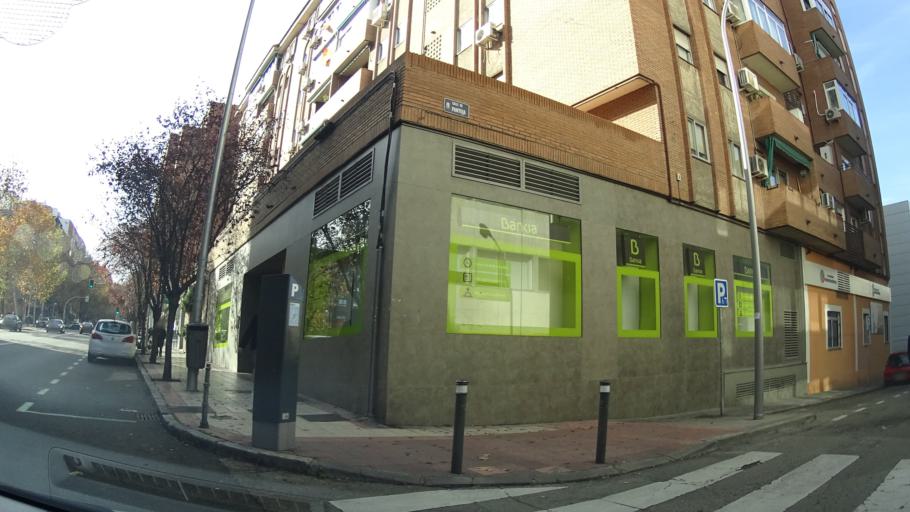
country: ES
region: Madrid
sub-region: Provincia de Madrid
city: Chamartin
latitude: 40.4470
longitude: -3.6699
